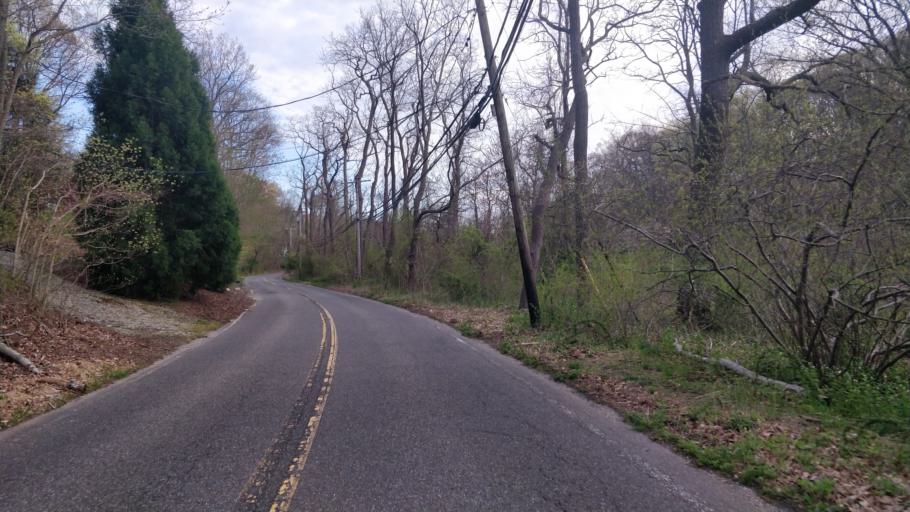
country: US
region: New York
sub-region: Suffolk County
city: Fort Salonga
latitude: 40.9126
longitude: -73.3127
